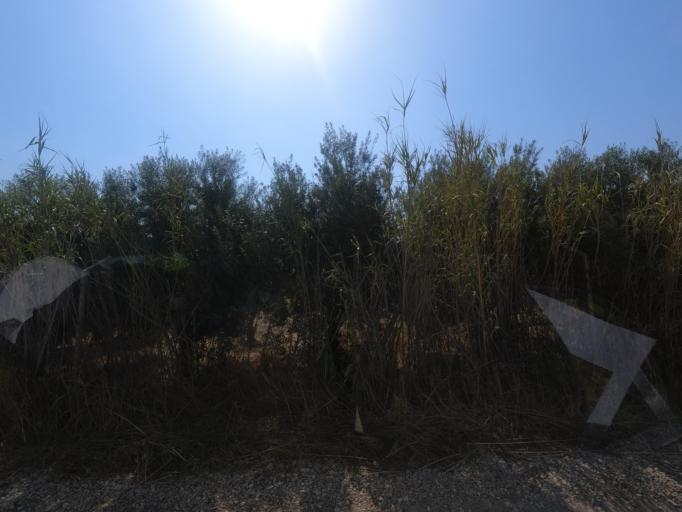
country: CY
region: Ammochostos
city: Avgorou
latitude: 35.0510
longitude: 33.8524
